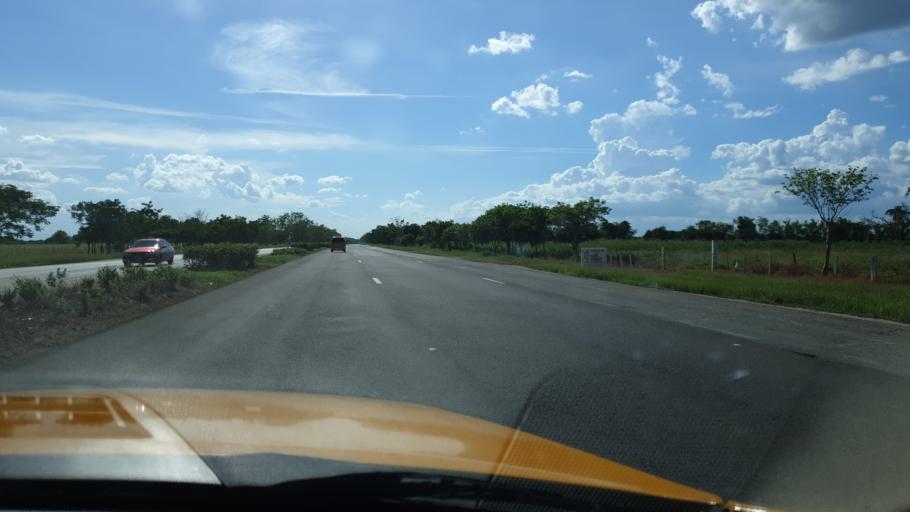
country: CU
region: Cienfuegos
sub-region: Municipio de Aguada de Pasajeros
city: Aguada de Pasajeros
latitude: 22.4103
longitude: -80.8918
